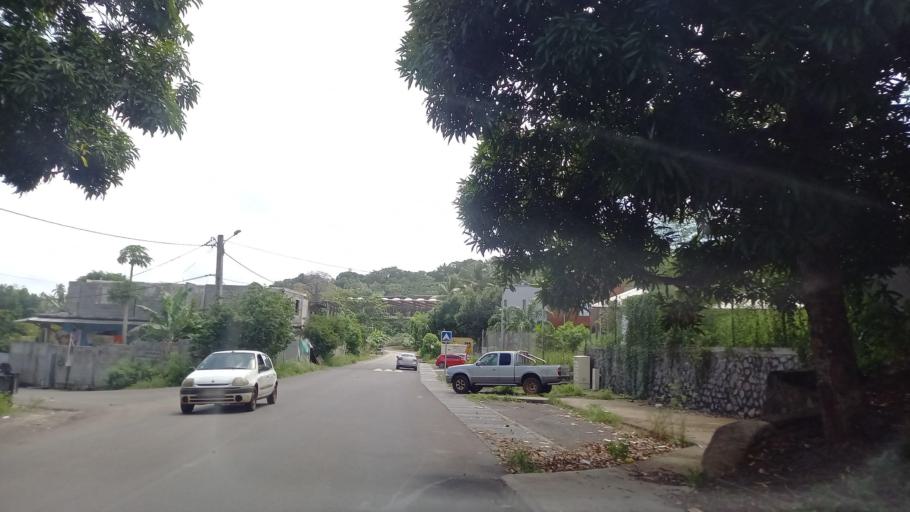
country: YT
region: Boueni
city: Boueni
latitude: -12.9247
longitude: 45.0916
